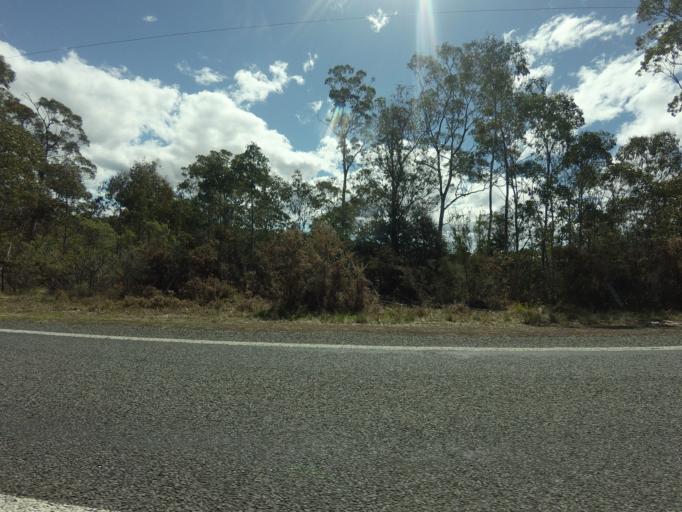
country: AU
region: Tasmania
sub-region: Northern Midlands
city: Evandale
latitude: -42.0304
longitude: 147.8326
